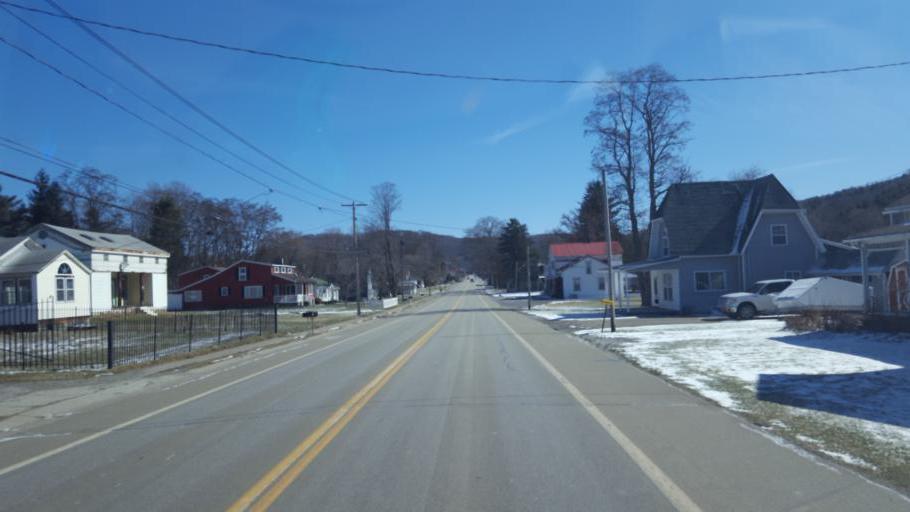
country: US
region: New York
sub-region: Allegany County
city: Andover
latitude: 42.0379
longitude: -77.7767
